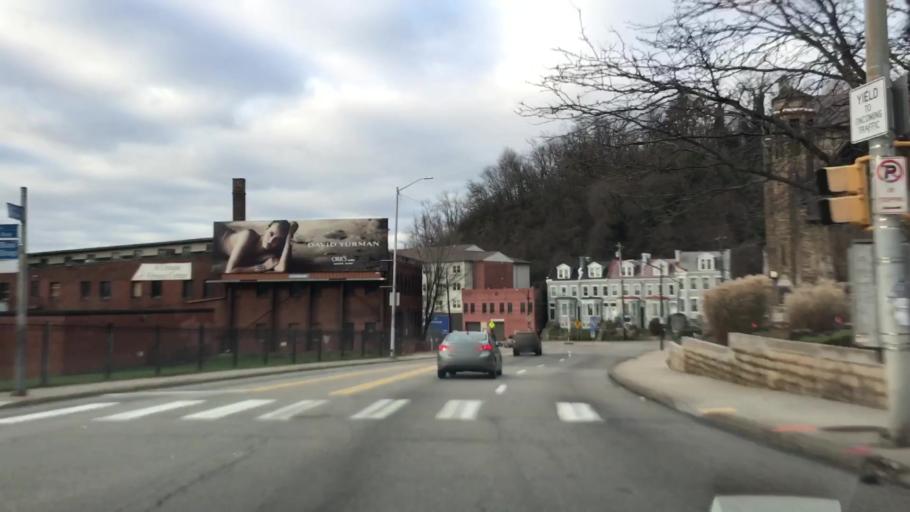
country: US
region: Pennsylvania
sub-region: Allegheny County
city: Bloomfield
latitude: 40.4379
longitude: -79.9639
